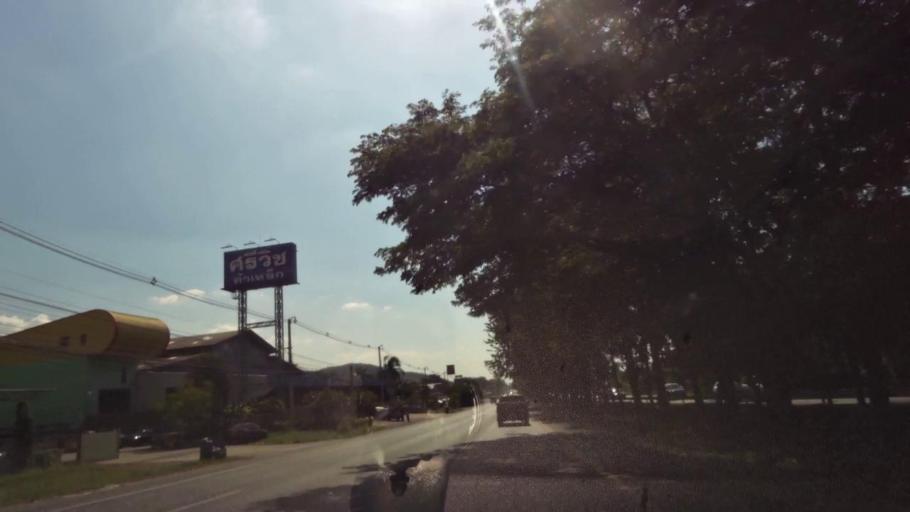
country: TH
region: Nakhon Sawan
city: Nakhon Sawan
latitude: 15.6394
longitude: 100.1327
